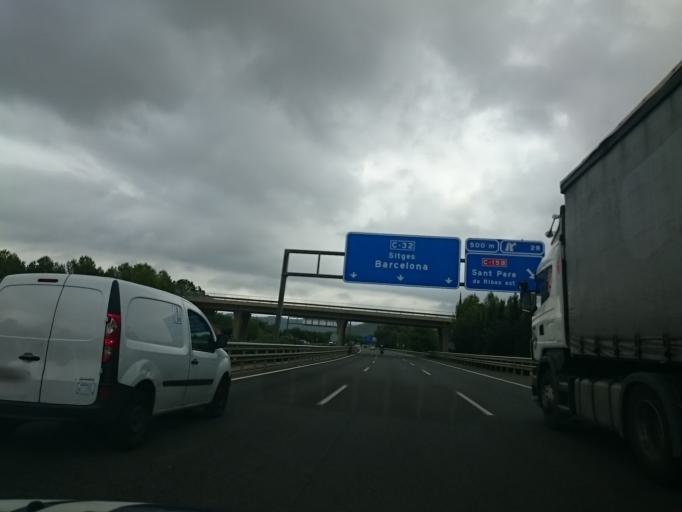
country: ES
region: Catalonia
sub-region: Provincia de Barcelona
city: Sant Pere de Ribes
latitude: 41.2466
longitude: 1.7797
